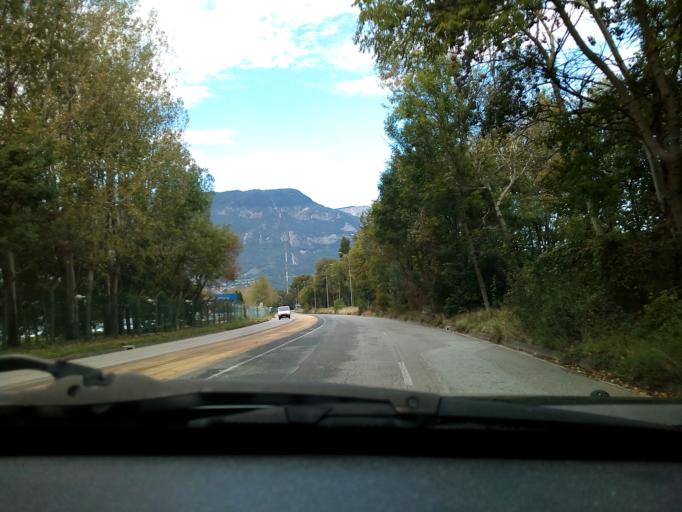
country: FR
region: Rhone-Alpes
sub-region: Departement de l'Isere
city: Fontaine
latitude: 45.2096
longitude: 5.6942
